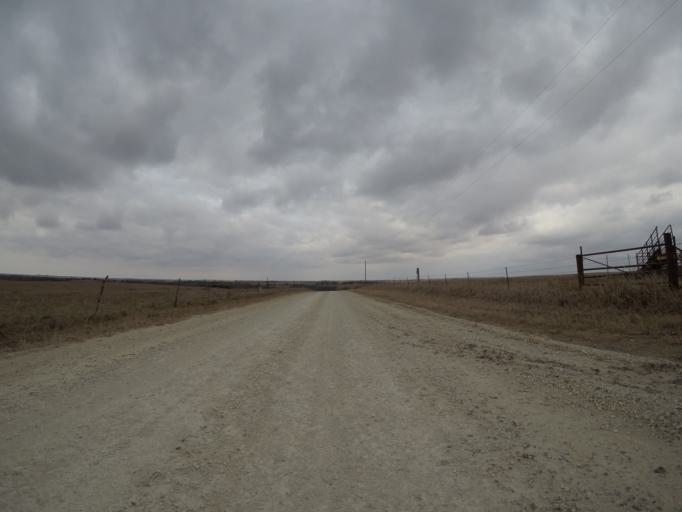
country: US
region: Kansas
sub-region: Morris County
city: Council Grove
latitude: 38.7578
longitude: -96.2794
